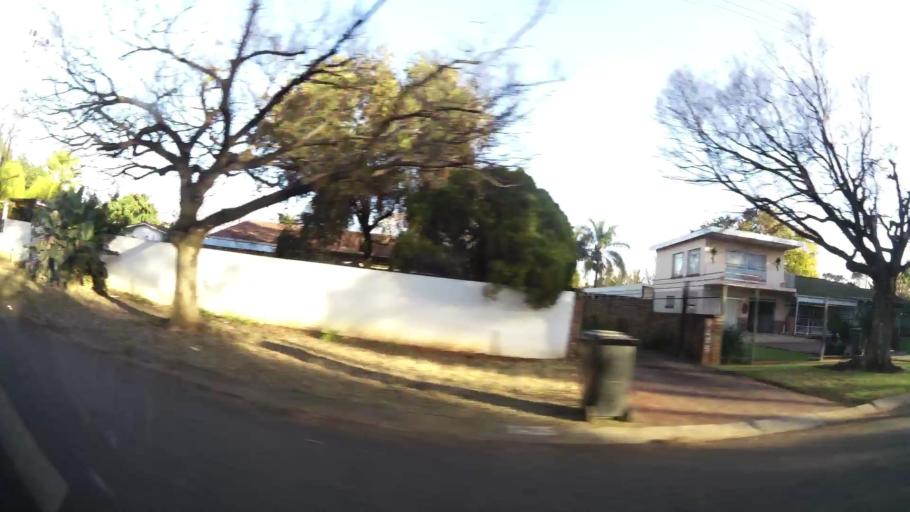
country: ZA
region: Gauteng
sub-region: City of Tshwane Metropolitan Municipality
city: Pretoria
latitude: -25.7050
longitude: 28.2647
